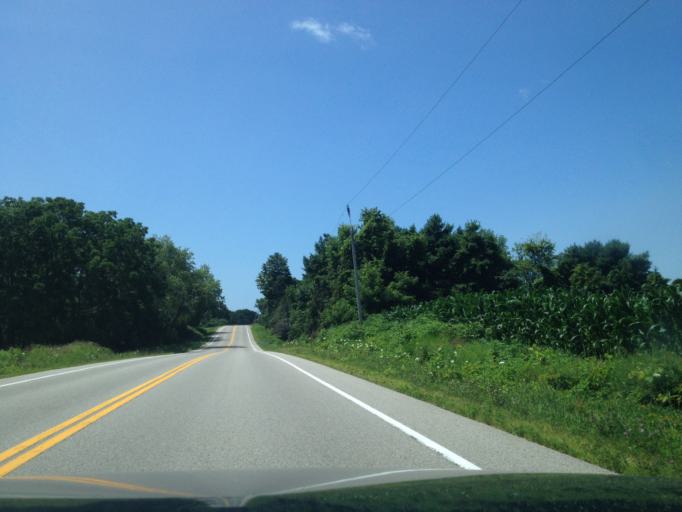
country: CA
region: Ontario
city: Norfolk County
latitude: 42.5827
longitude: -80.5223
